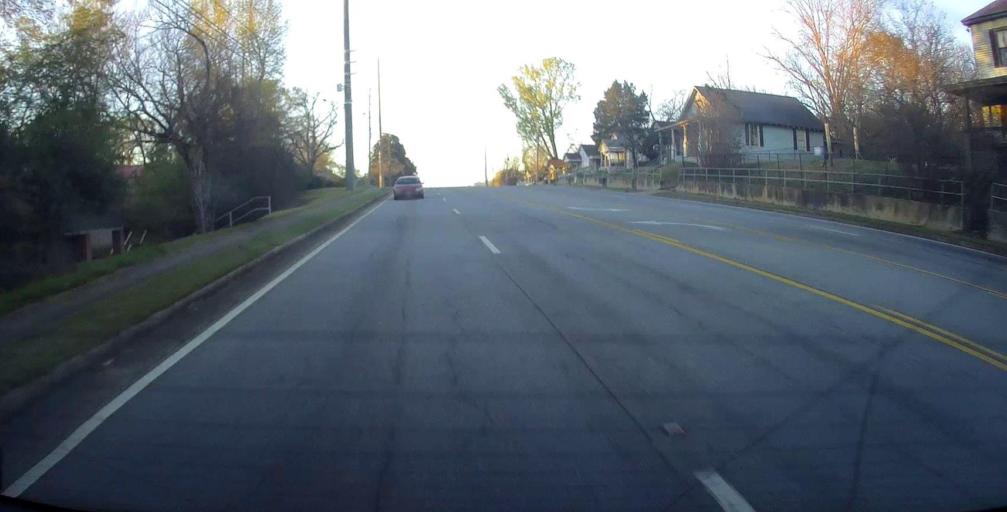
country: US
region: Alabama
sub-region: Russell County
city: Phenix City
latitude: 32.5012
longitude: -84.9901
